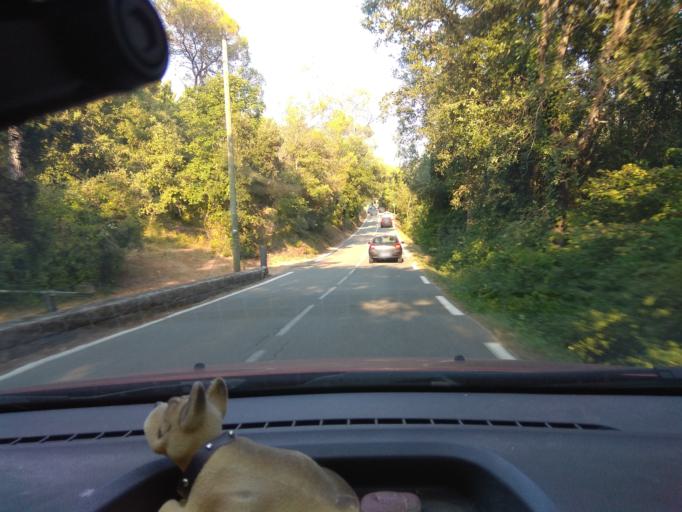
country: FR
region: Provence-Alpes-Cote d'Azur
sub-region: Departement des Alpes-Maritimes
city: Le Rouret
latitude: 43.6614
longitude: 7.0346
